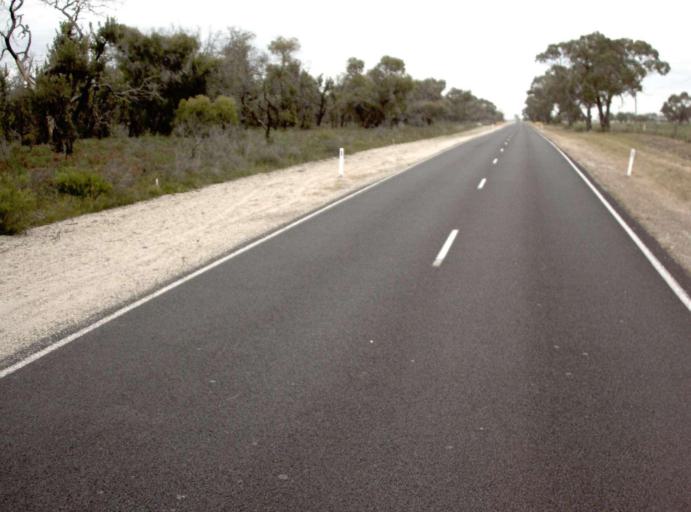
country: AU
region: Victoria
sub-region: Wellington
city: Sale
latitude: -38.1411
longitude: 147.4054
